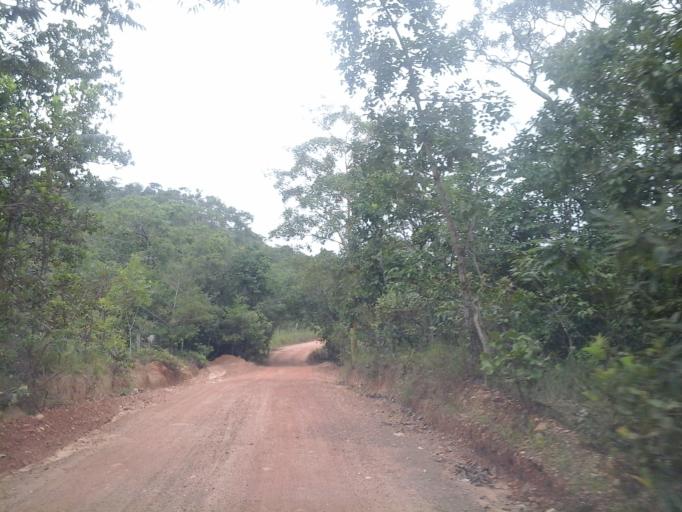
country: BR
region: Goias
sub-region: Pirenopolis
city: Pirenopolis
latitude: -15.7463
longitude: -49.0427
